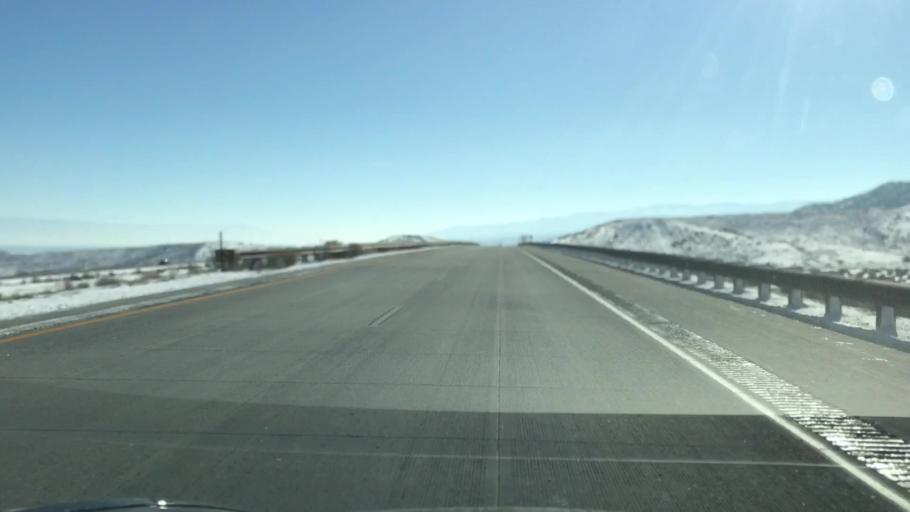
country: US
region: Colorado
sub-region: Mesa County
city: Loma
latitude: 39.1948
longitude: -108.8453
